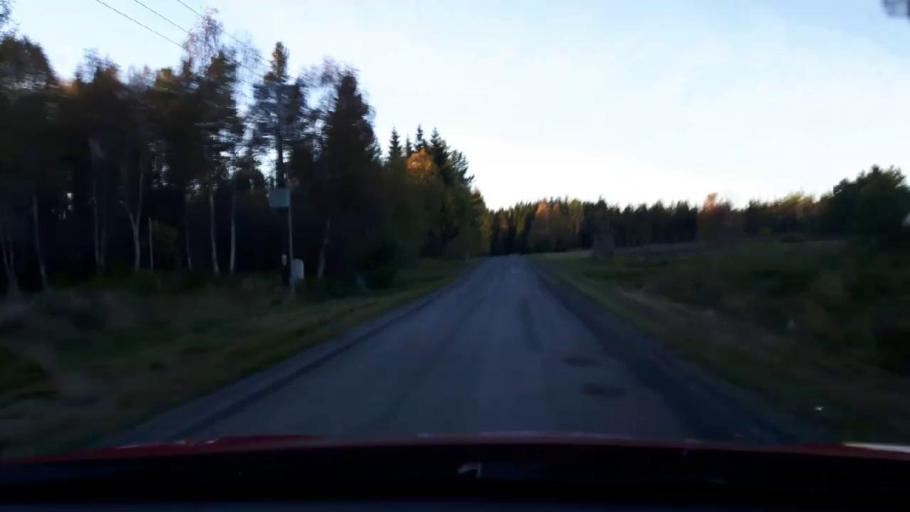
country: SE
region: Jaemtland
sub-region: Krokoms Kommun
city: Krokom
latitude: 63.4521
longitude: 14.4158
